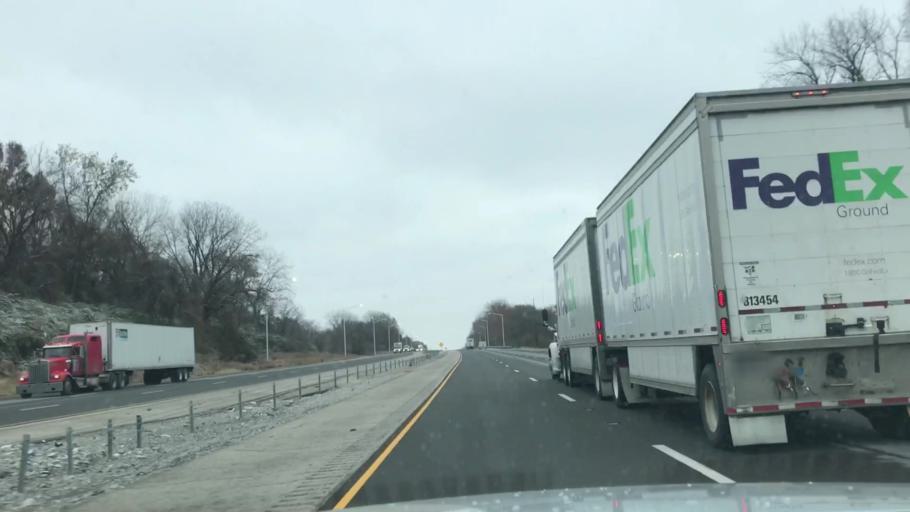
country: US
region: Illinois
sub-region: Madison County
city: Glen Carbon
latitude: 38.7565
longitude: -90.0043
